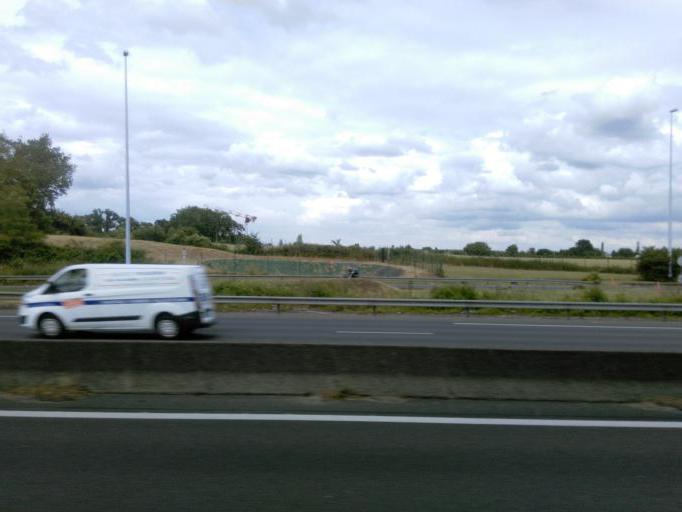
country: FR
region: Ile-de-France
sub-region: Departement du Val-d'Oise
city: Pierrelaye
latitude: 49.0160
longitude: 2.1441
